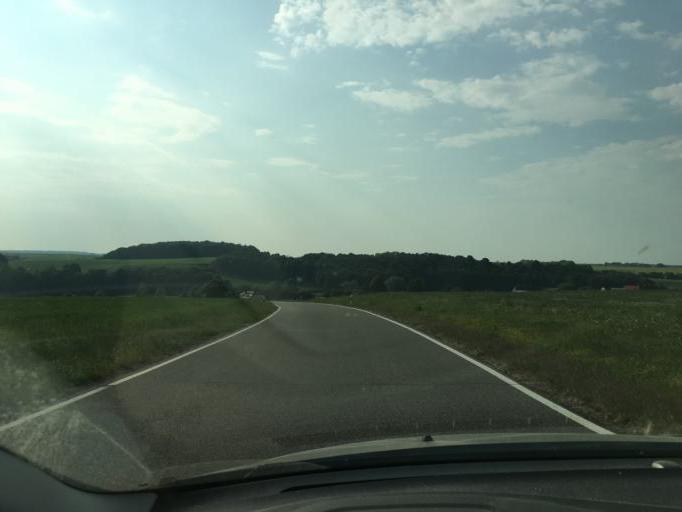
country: DE
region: Saxony
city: Rochlitz
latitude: 51.0666
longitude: 12.7971
